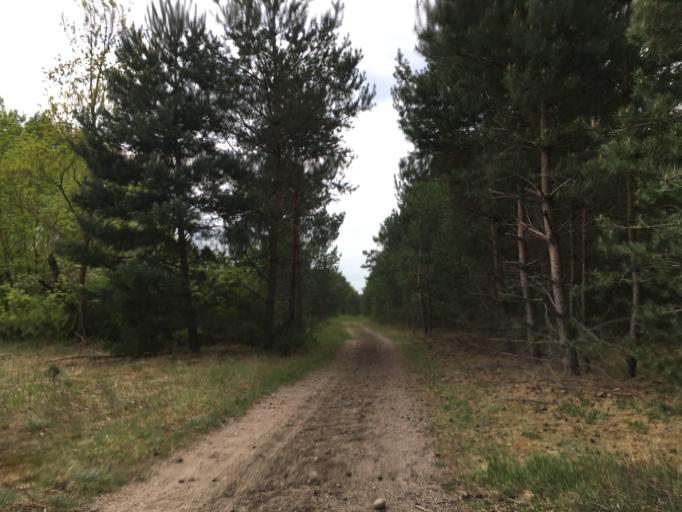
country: DE
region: Brandenburg
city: Rudnitz
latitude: 52.6970
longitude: 13.6139
